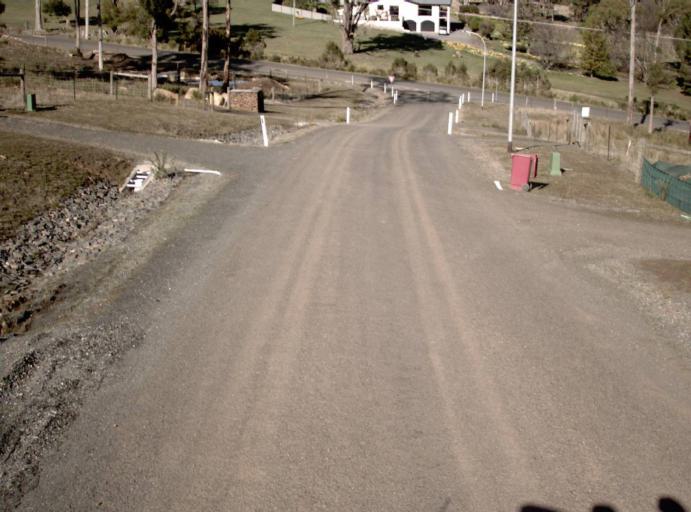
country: AU
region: Tasmania
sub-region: Launceston
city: Mayfield
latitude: -41.2816
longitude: 147.0352
